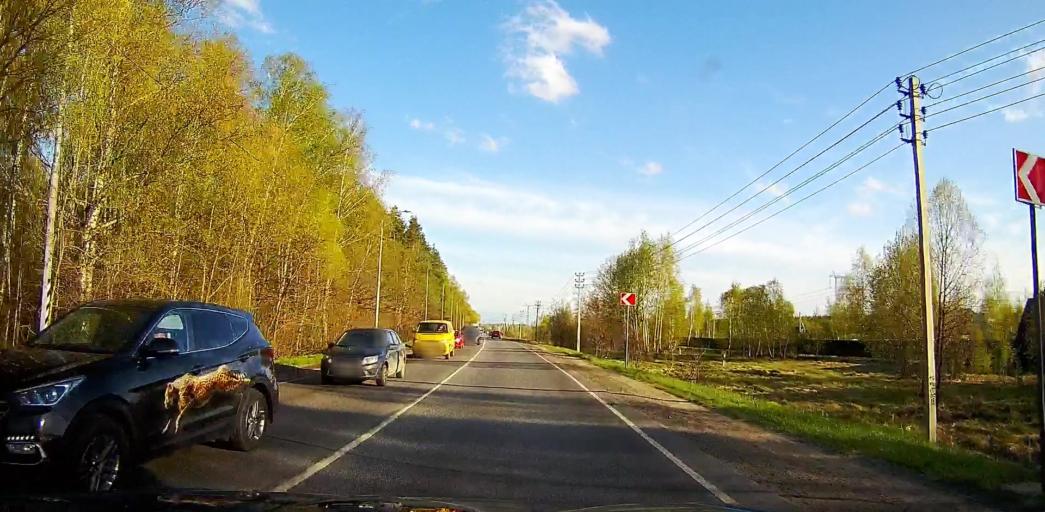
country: RU
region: Moskovskaya
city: Bronnitsy
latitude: 55.3805
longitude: 38.2084
